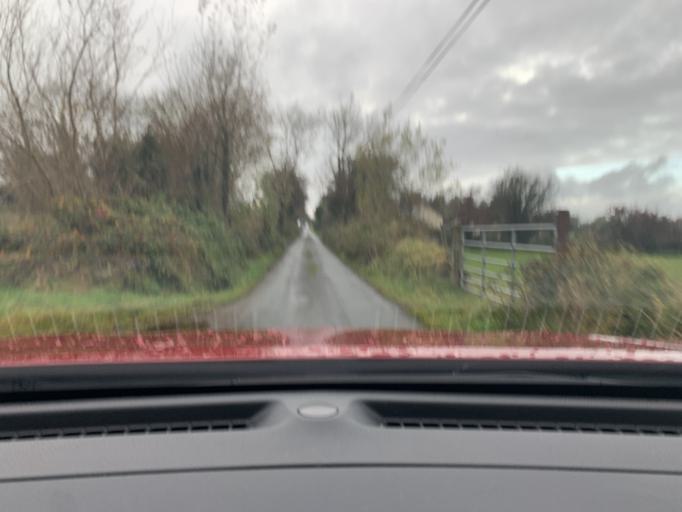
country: IE
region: Connaught
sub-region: Roscommon
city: Ballaghaderreen
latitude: 53.9666
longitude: -8.5662
